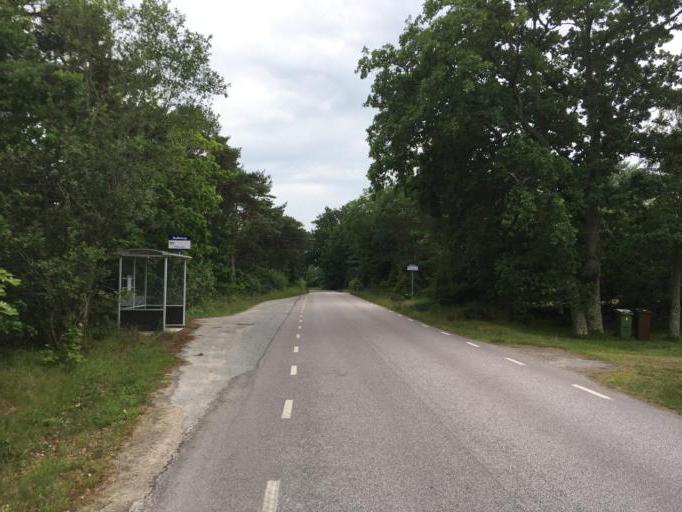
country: SE
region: Blekinge
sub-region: Karlskrona Kommun
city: Sturko
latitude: 56.0948
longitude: 15.6945
